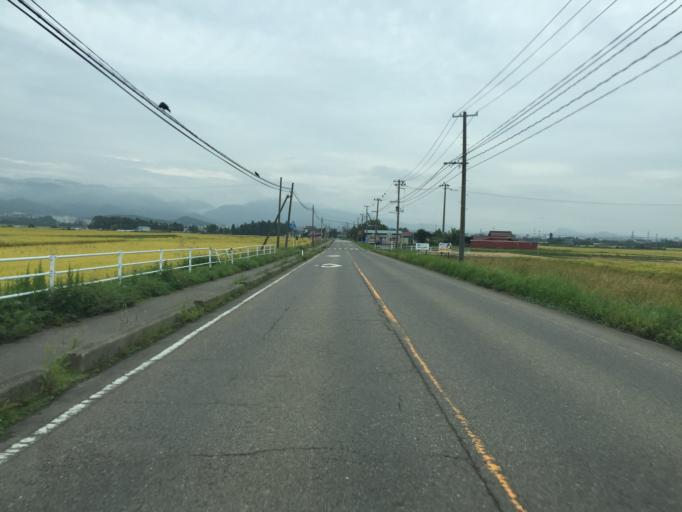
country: JP
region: Fukushima
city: Kitakata
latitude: 37.5414
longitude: 139.9290
